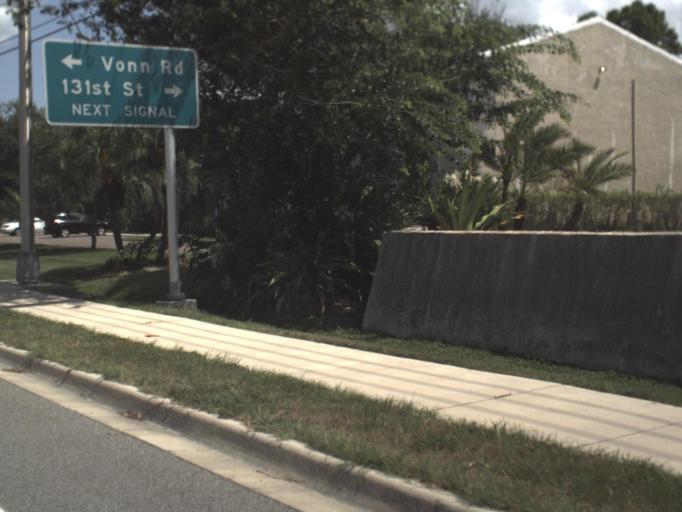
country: US
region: Florida
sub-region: Pinellas County
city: Ridgecrest
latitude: 27.8802
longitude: -82.8231
